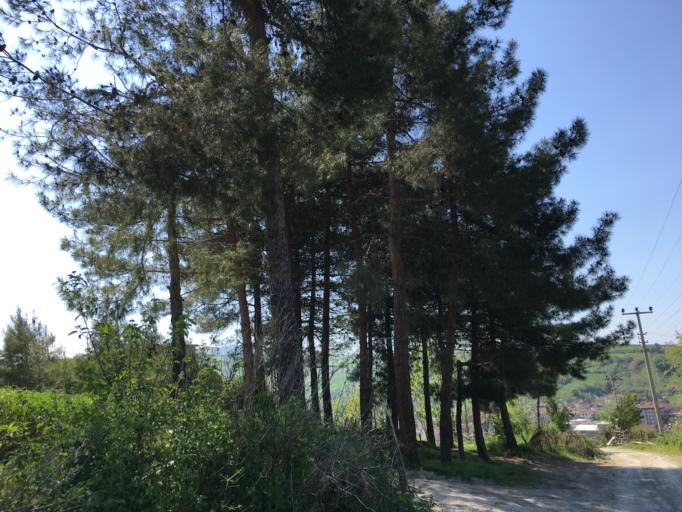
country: TR
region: Samsun
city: Alacam
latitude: 41.6066
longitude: 35.6053
